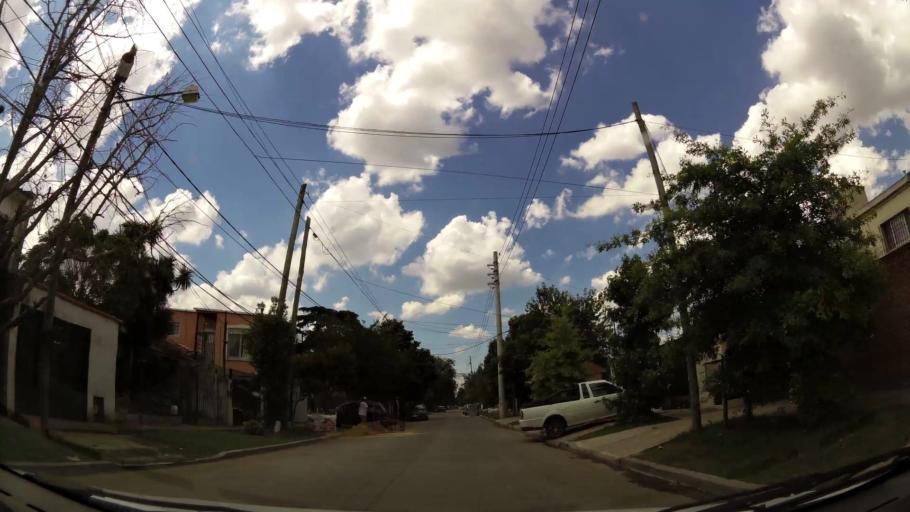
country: AR
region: Buenos Aires
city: Ituzaingo
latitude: -34.6477
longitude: -58.6864
